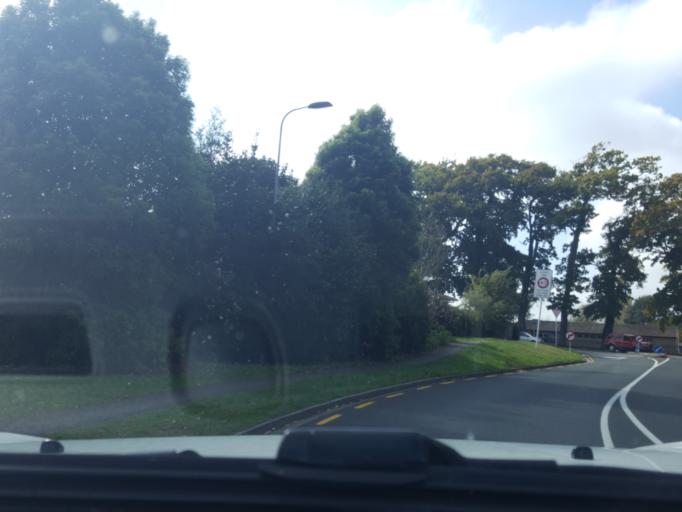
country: NZ
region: Waikato
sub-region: Hamilton City
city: Hamilton
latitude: -37.7491
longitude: 175.2774
